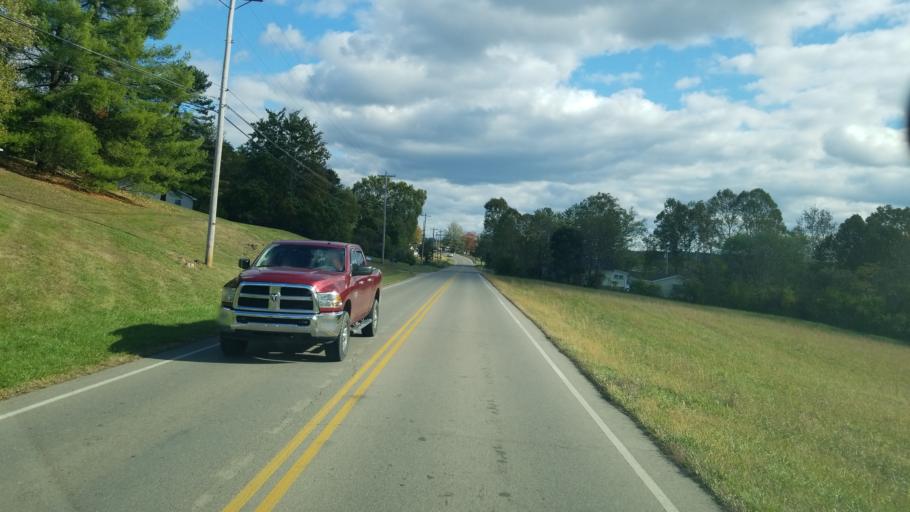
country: US
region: Ohio
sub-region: Jackson County
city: Wellston
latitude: 39.1136
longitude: -82.5458
